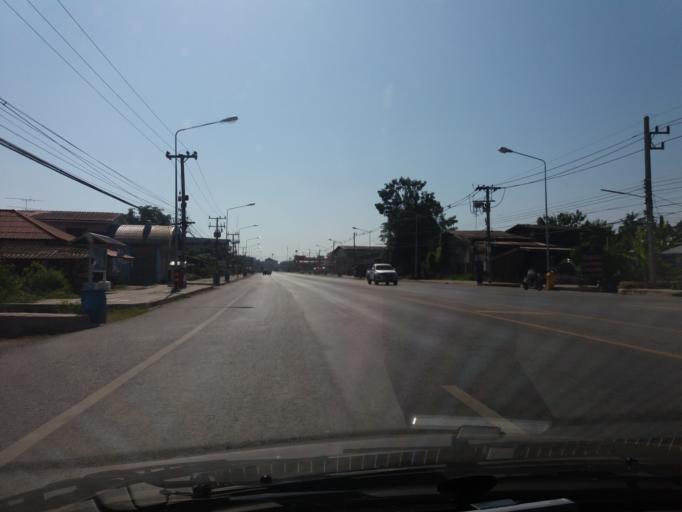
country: TH
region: Kamphaeng Phet
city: Khlong Khlung
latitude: 16.2408
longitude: 99.7266
